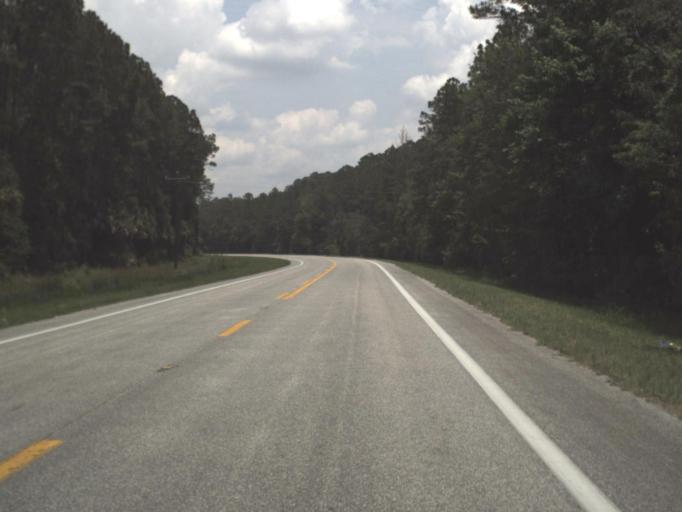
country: US
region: Florida
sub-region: Putnam County
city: Palatka
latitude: 29.5474
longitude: -81.7432
